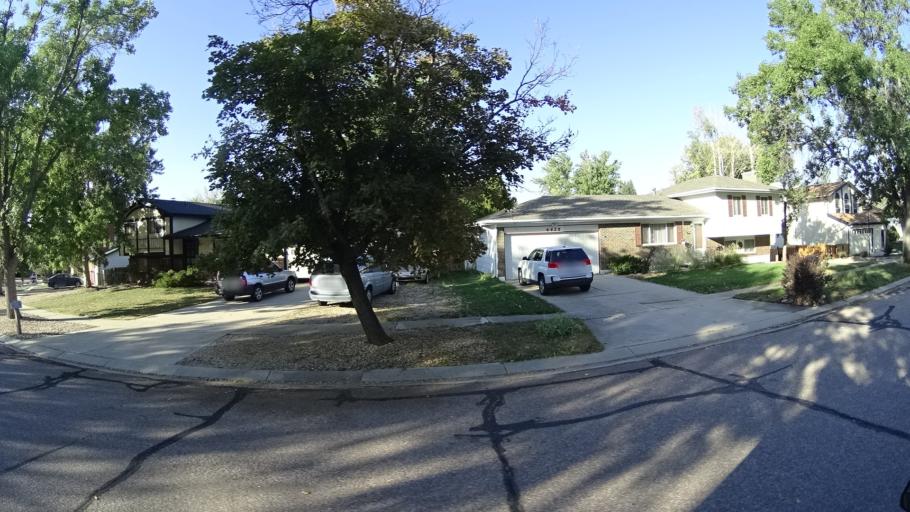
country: US
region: Colorado
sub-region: El Paso County
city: Cimarron Hills
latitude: 38.8839
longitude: -104.7456
